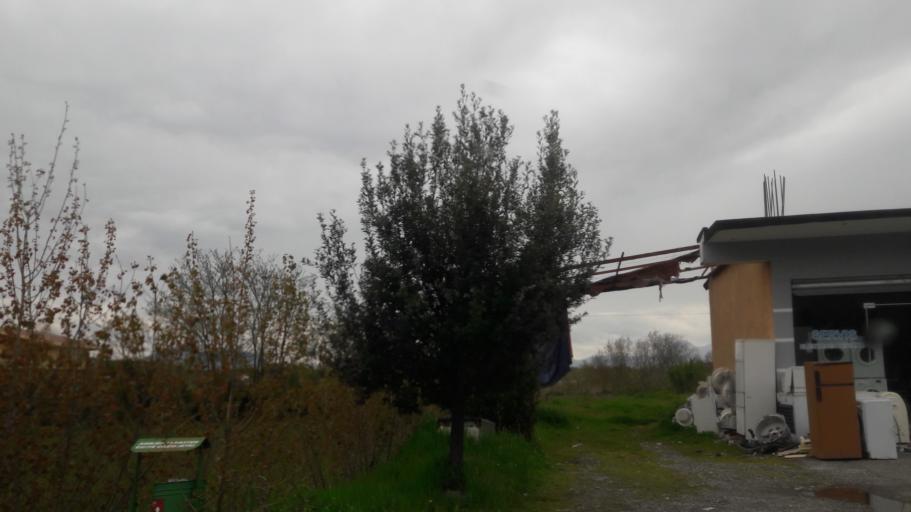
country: AL
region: Shkoder
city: Vukatane
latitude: 41.9603
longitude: 19.5361
